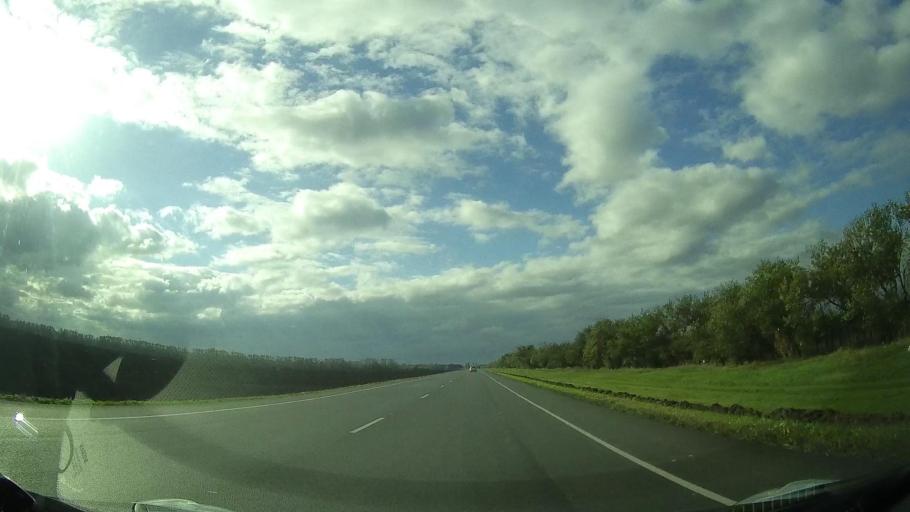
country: RU
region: Rostov
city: Tselina
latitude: 46.5325
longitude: 40.9327
